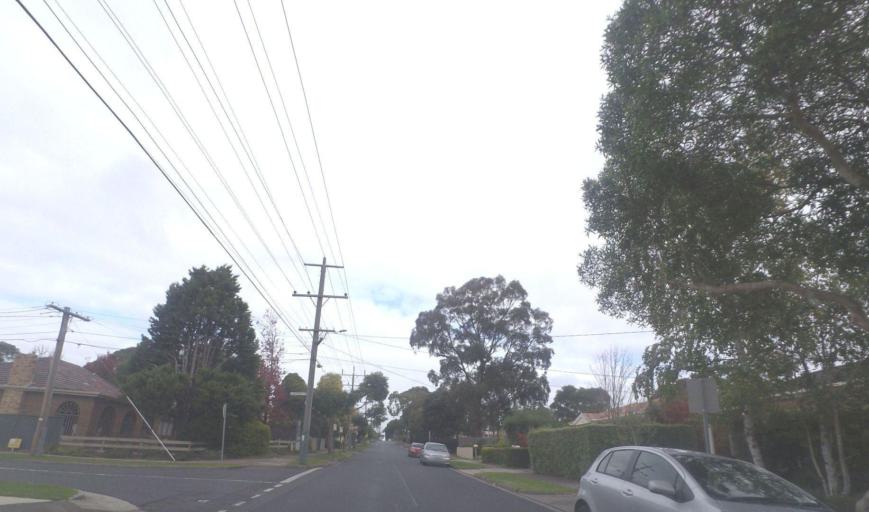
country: AU
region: Victoria
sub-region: Whitehorse
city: Blackburn North
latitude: -37.8060
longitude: 145.1529
